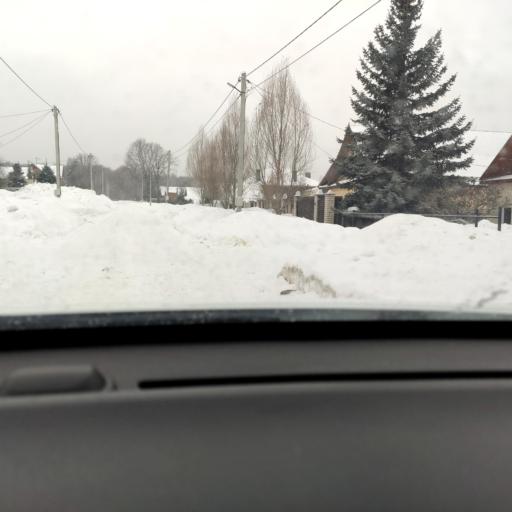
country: RU
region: Tatarstan
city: Stolbishchi
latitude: 55.6744
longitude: 49.1149
